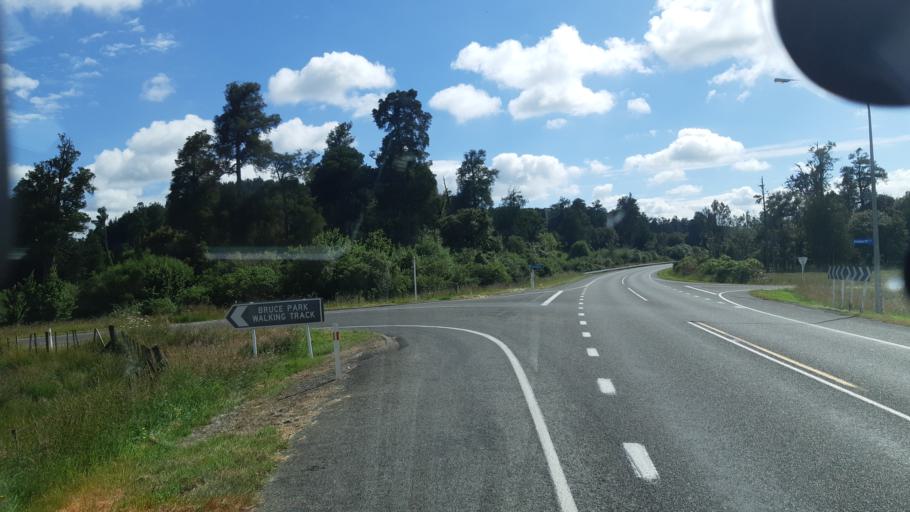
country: NZ
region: Manawatu-Wanganui
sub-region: Rangitikei District
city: Bulls
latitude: -39.9655
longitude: 175.5246
